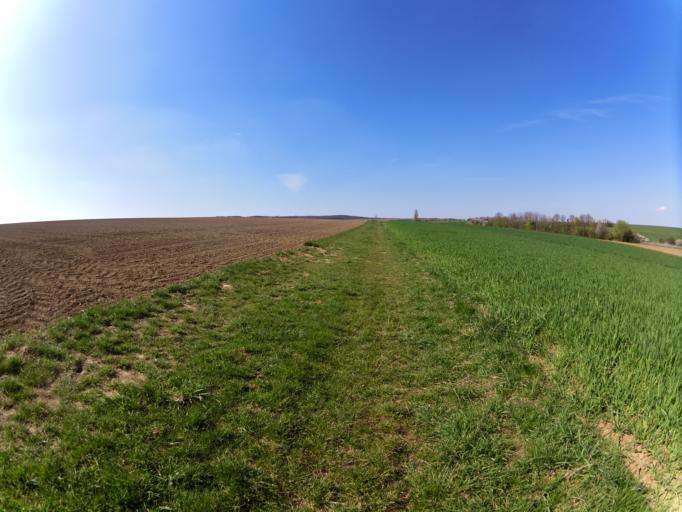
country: DE
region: Bavaria
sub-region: Regierungsbezirk Unterfranken
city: Kurnach
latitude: 49.8672
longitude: 10.0135
